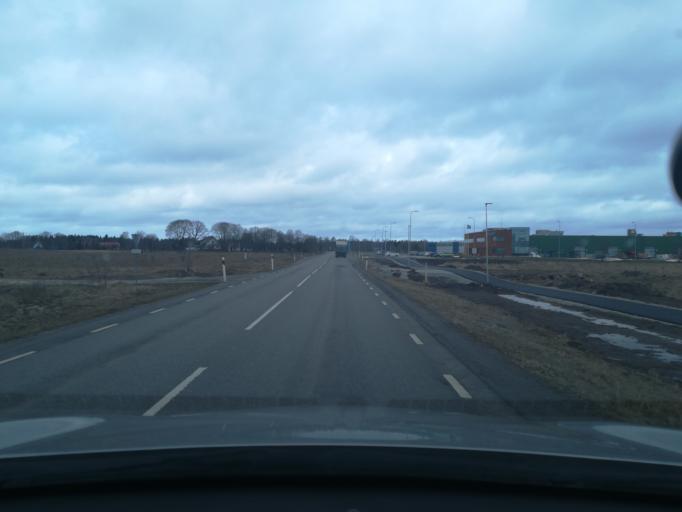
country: EE
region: Harju
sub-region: Harku vald
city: Tabasalu
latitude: 59.4181
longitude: 24.5428
